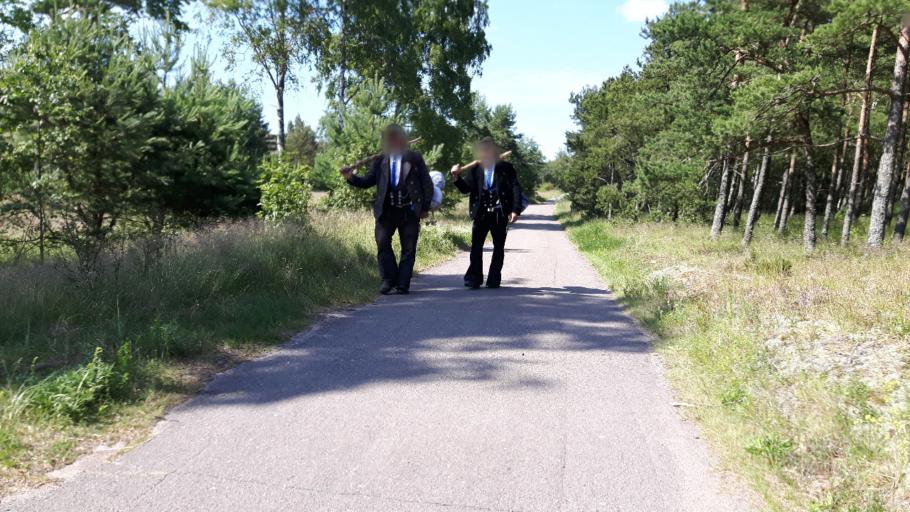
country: LT
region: Klaipedos apskritis
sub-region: Klaipeda
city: Klaipeda
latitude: 55.6834
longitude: 21.1043
